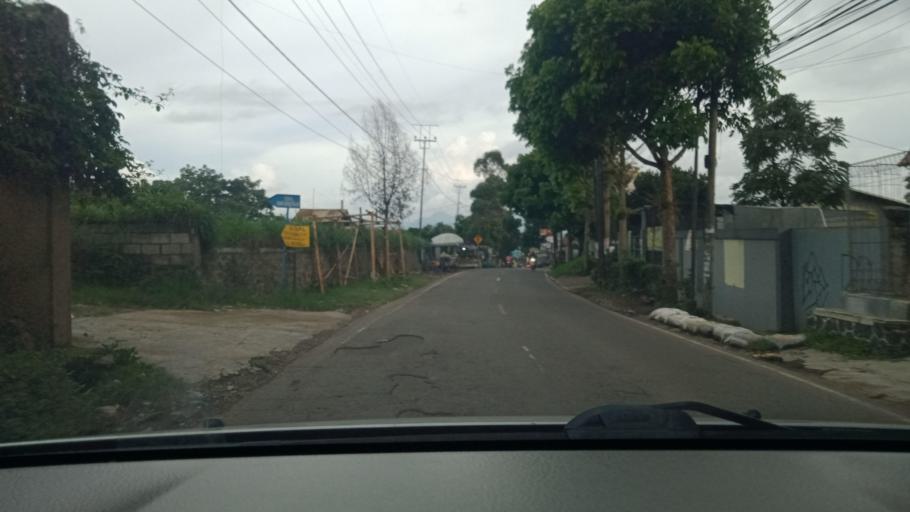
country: ID
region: West Java
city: Lembang
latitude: -6.8057
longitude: 107.5949
